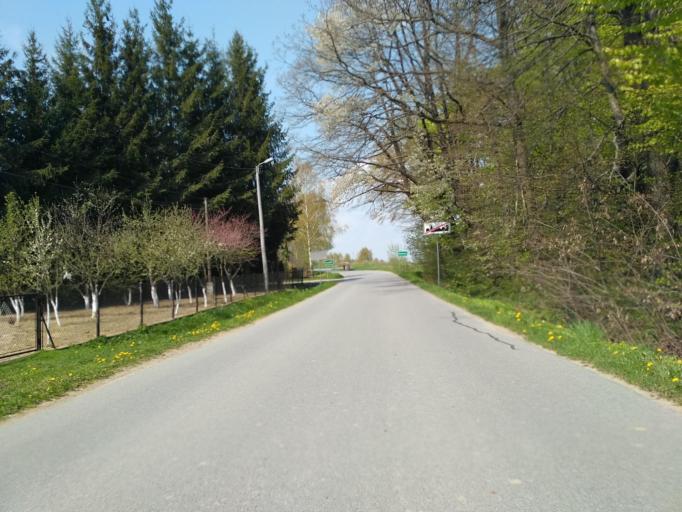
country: PL
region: Subcarpathian Voivodeship
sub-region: Powiat jasielski
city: Osiek Jasielski
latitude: 49.6738
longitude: 21.5235
